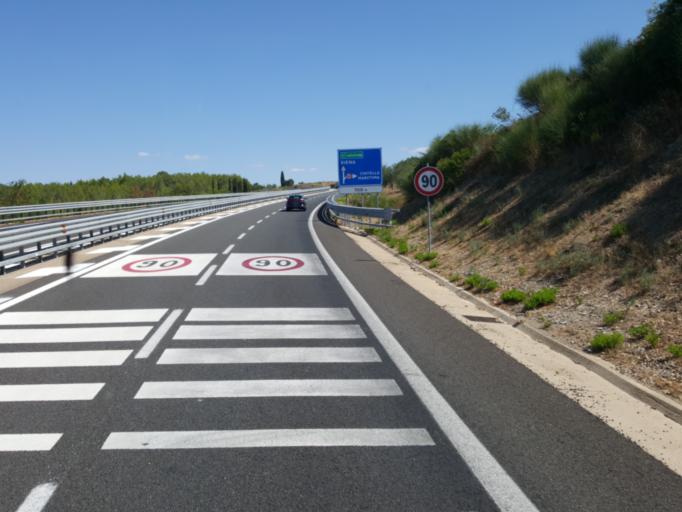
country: IT
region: Tuscany
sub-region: Provincia di Grosseto
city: Civitella Marittima
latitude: 42.9889
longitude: 11.2868
